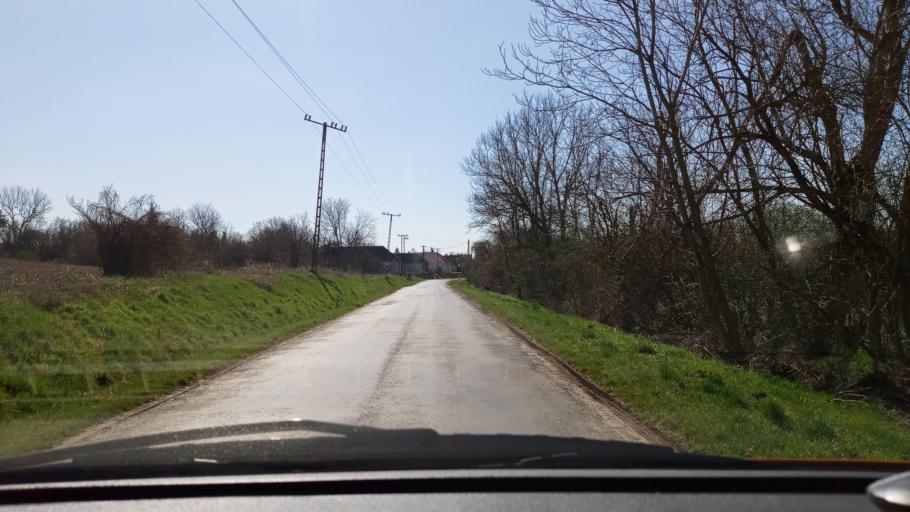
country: HU
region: Baranya
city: Kozarmisleny
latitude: 46.0642
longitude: 18.3722
